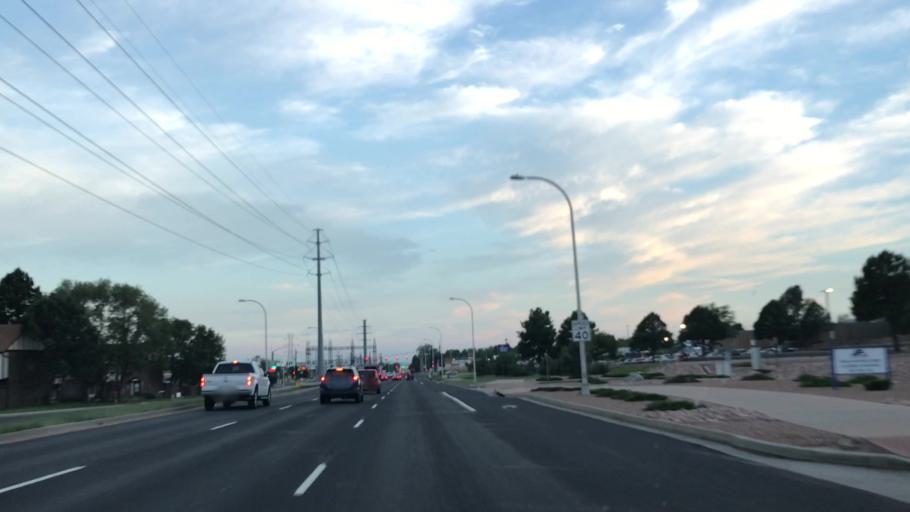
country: US
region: Colorado
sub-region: El Paso County
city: Cimarron Hills
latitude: 38.8622
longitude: -104.7574
